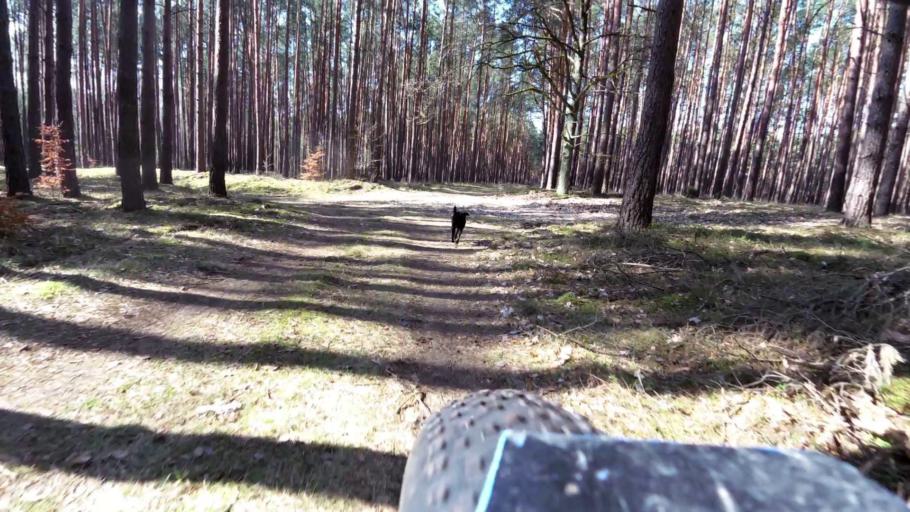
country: PL
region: Lubusz
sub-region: Powiat slubicki
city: Cybinka
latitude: 52.2092
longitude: 14.9015
